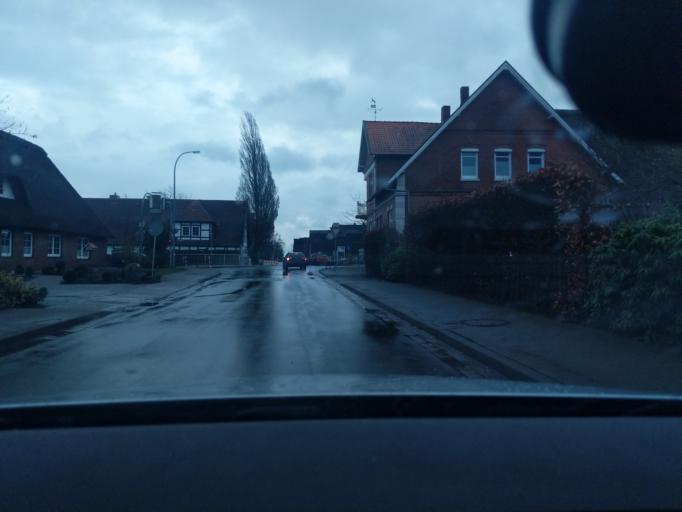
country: DE
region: Lower Saxony
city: Jork
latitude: 53.5186
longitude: 9.6703
